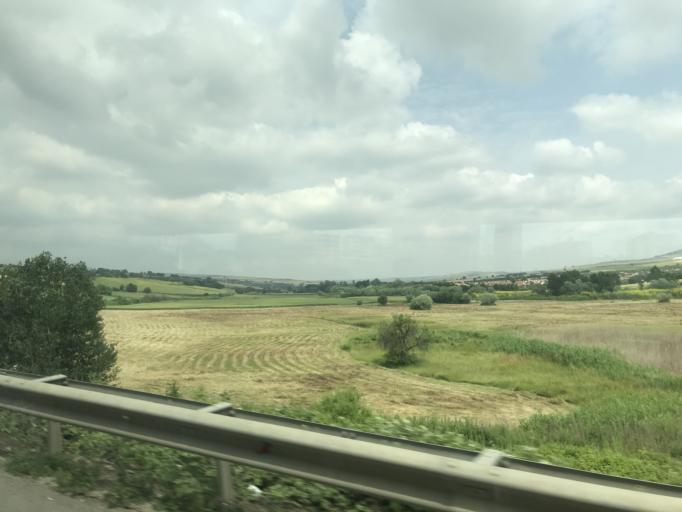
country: TR
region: Tekirdag
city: Tekirdag
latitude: 40.9906
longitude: 27.5699
